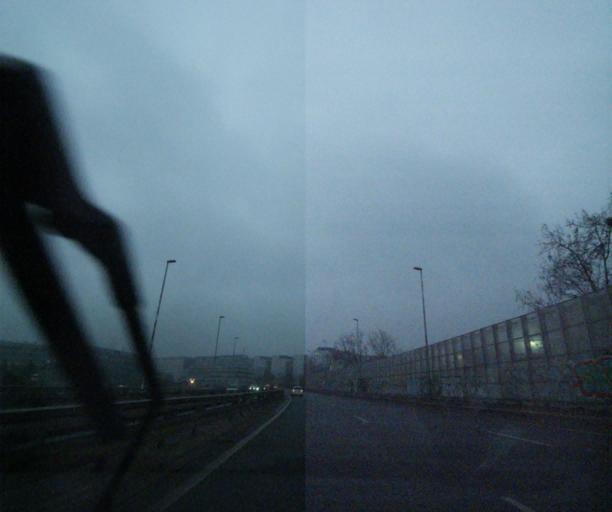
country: FR
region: Ile-de-France
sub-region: Departement des Hauts-de-Seine
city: Nanterre
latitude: 48.9015
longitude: 2.2193
